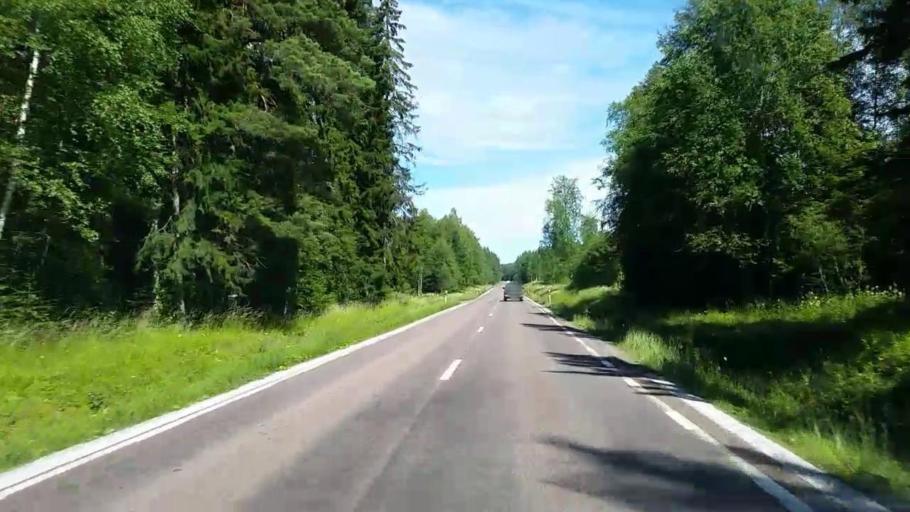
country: SE
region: Dalarna
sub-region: Rattviks Kommun
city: Raettvik
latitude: 60.9031
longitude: 15.1882
